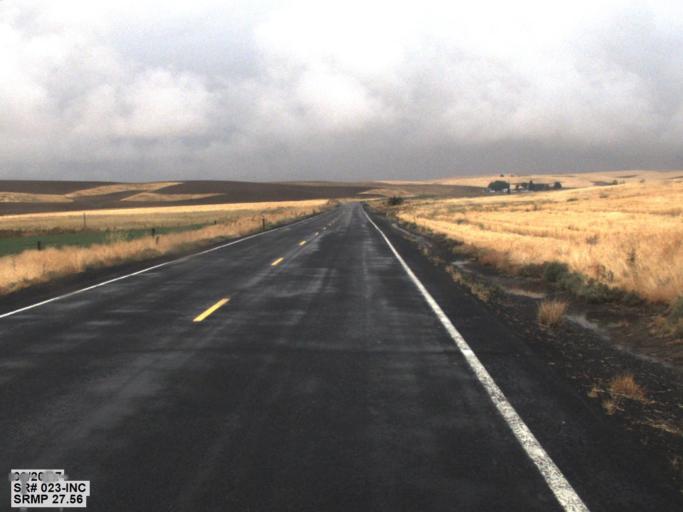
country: US
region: Washington
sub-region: Spokane County
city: Cheney
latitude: 47.1216
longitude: -117.8261
